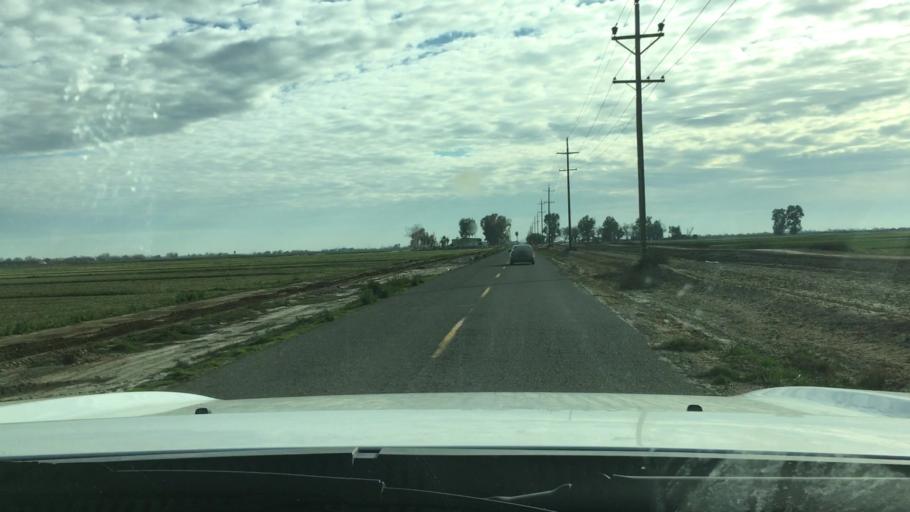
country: US
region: California
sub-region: Kings County
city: Stratford
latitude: 36.2258
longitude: -119.7688
